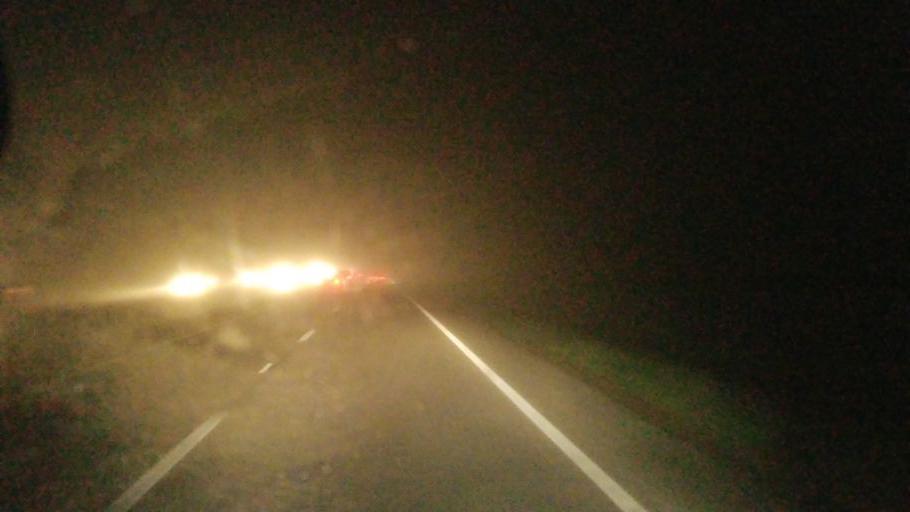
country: US
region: Ohio
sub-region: Pickaway County
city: Commercial Point
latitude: 39.8108
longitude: -82.9963
